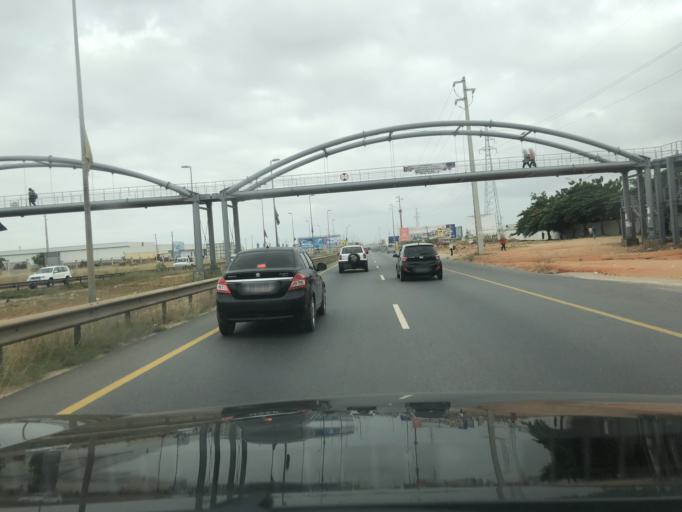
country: AO
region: Luanda
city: Luanda
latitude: -8.9734
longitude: 13.2336
